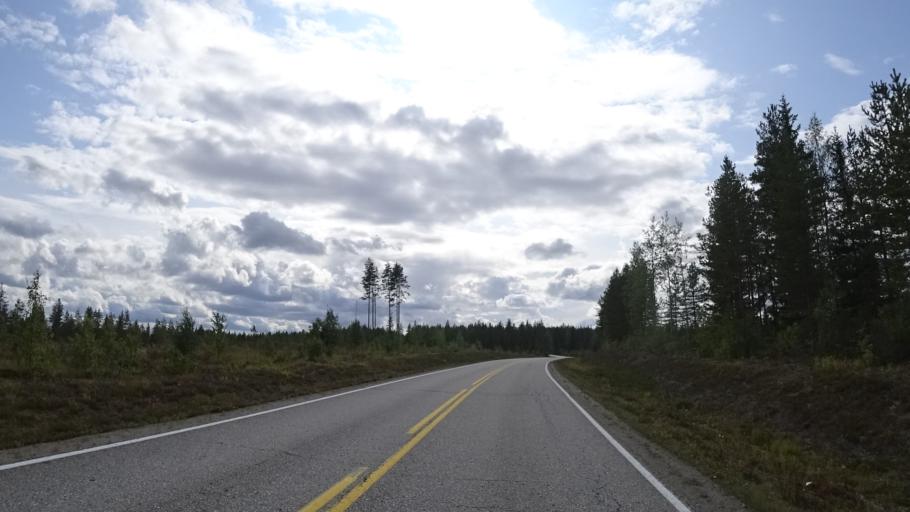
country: FI
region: North Karelia
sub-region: Joensuu
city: Ilomantsi
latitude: 62.7934
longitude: 31.1039
